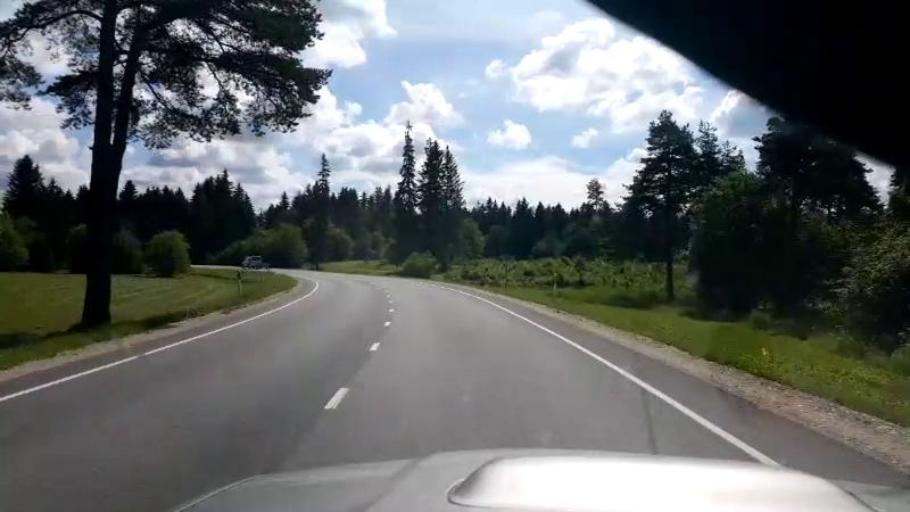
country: EE
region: Laeaene-Virumaa
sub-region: Tapa vald
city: Tapa
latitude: 59.2551
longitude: 25.9635
